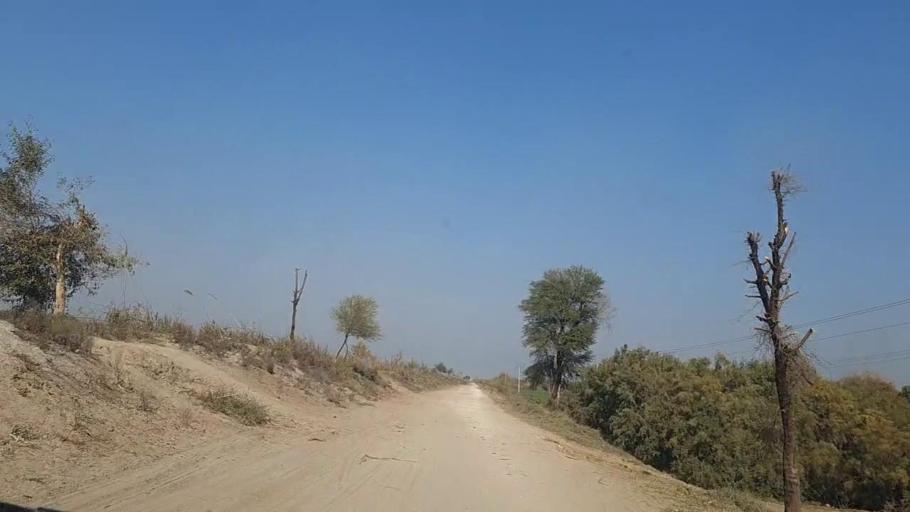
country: PK
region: Sindh
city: Sakrand
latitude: 26.0651
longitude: 68.3494
